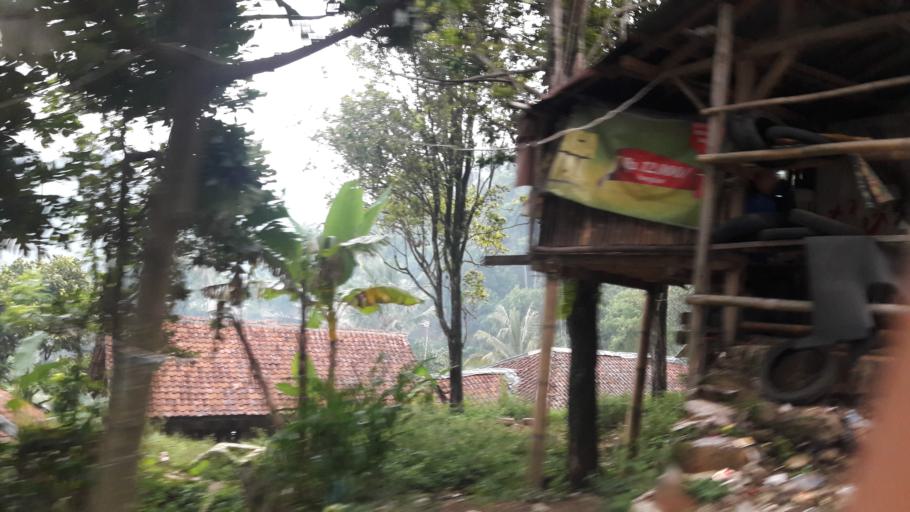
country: ID
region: West Java
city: Cipeundeuy
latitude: -6.6777
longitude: 106.5272
